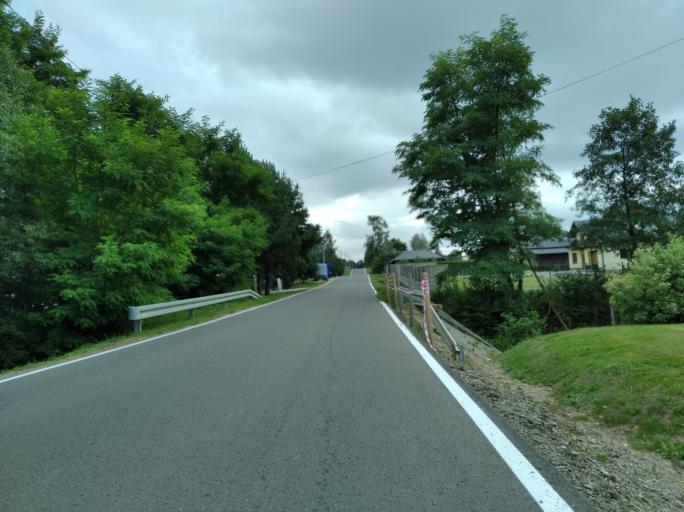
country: PL
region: Subcarpathian Voivodeship
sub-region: Powiat krosnienski
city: Odrzykon
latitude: 49.7433
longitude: 21.7295
